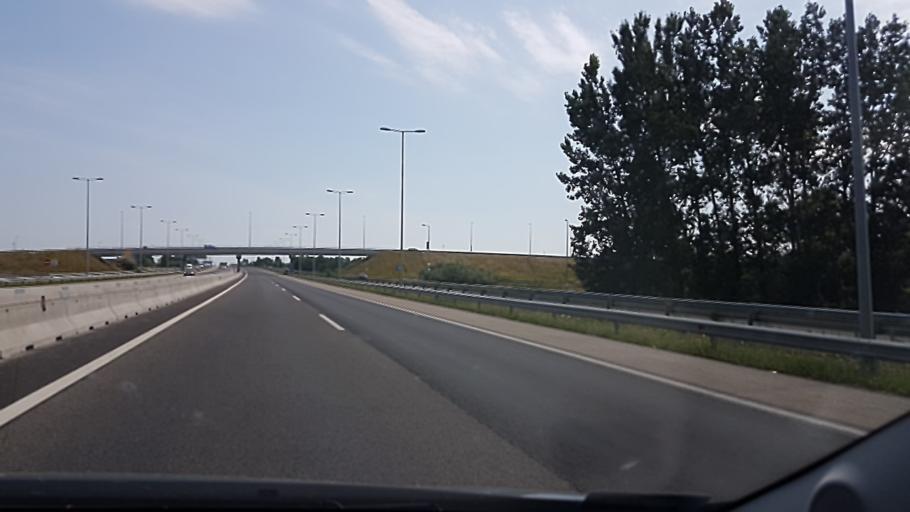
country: HU
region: Budapest
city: Budapest XVIII. keruelet
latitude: 47.4163
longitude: 19.1546
